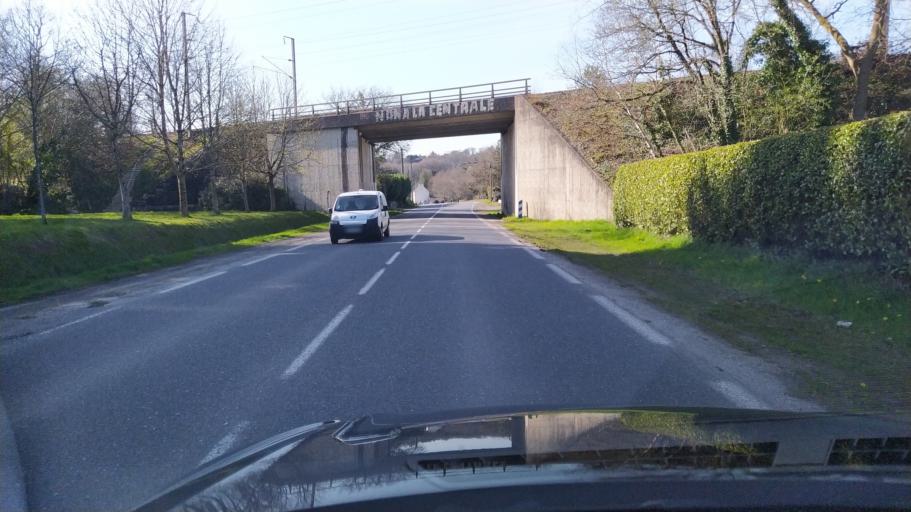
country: FR
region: Brittany
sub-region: Departement du Finistere
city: Lampaul-Guimiliau
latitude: 48.4972
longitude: -4.0542
